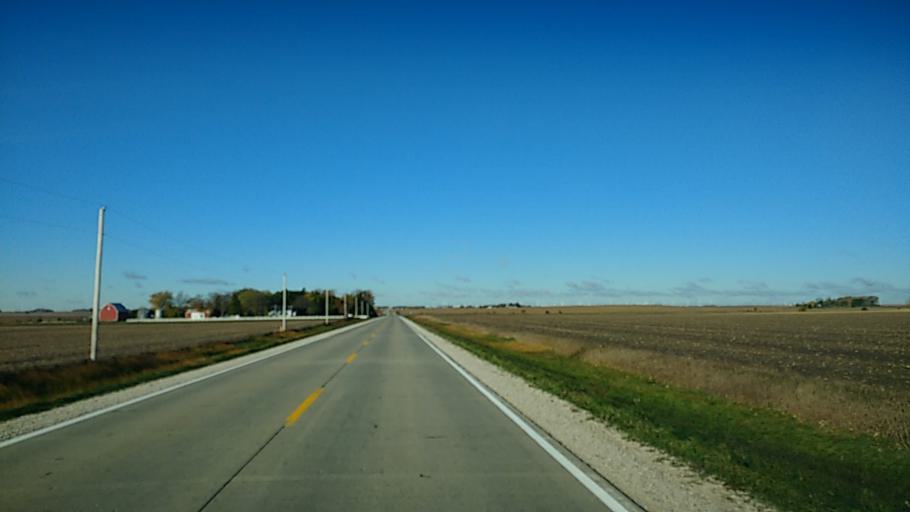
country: US
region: Iowa
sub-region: Buena Vista County
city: Storm Lake
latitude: 42.5182
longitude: -95.1930
